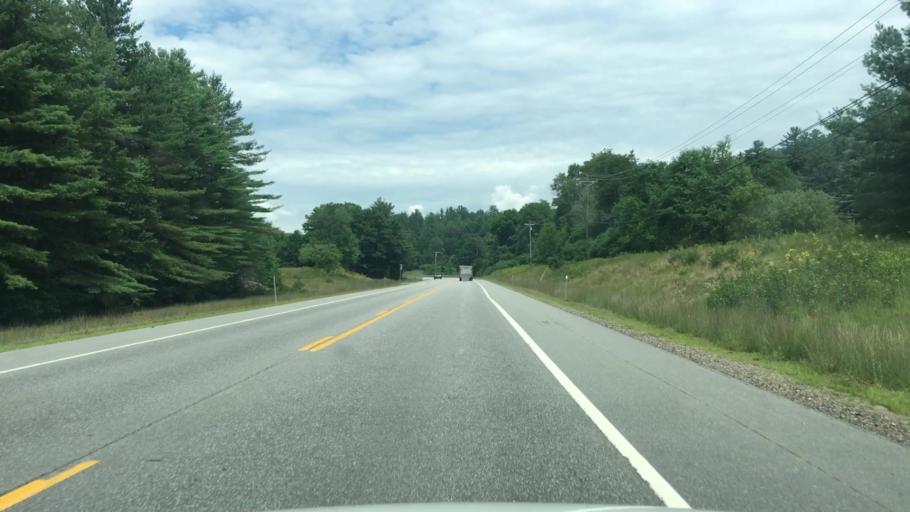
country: US
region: New Hampshire
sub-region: Grafton County
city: Rumney
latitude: 43.8528
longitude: -71.9109
